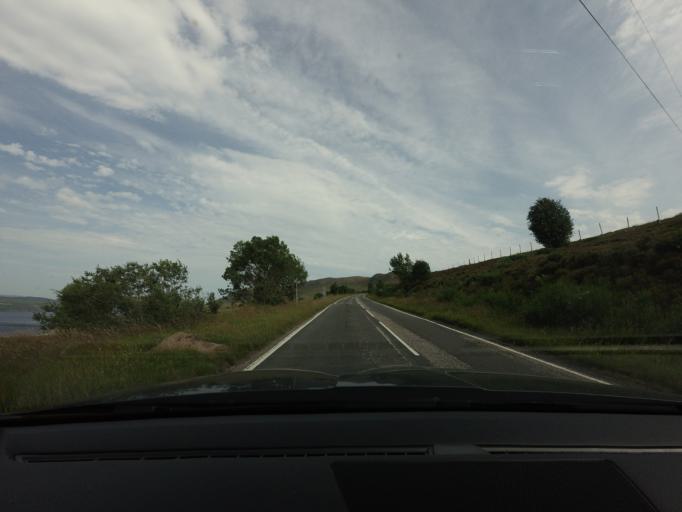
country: GB
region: Scotland
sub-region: Highland
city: Alness
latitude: 57.8431
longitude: -4.2840
